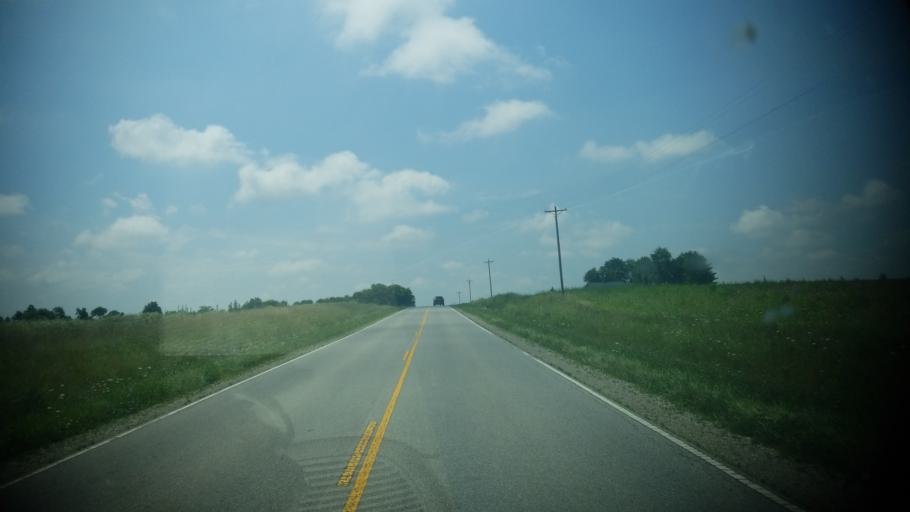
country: US
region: Illinois
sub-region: Wayne County
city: Fairfield
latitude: 38.4371
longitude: -88.3495
